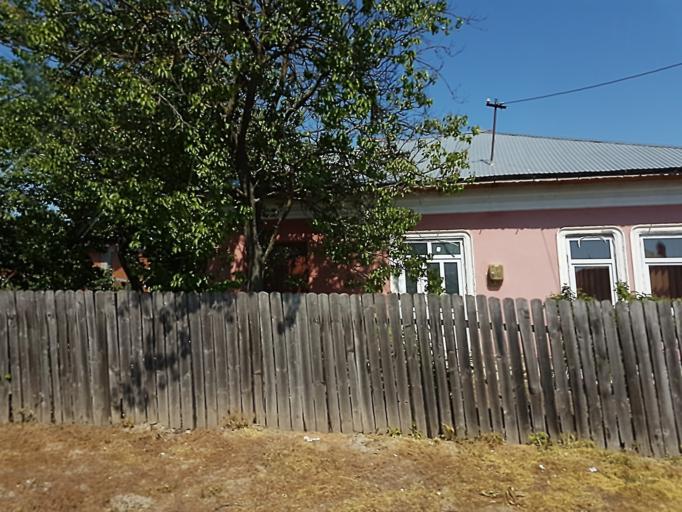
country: RO
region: Giurgiu
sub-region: Comuna Herasti
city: Herasti
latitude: 44.2124
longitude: 26.3603
